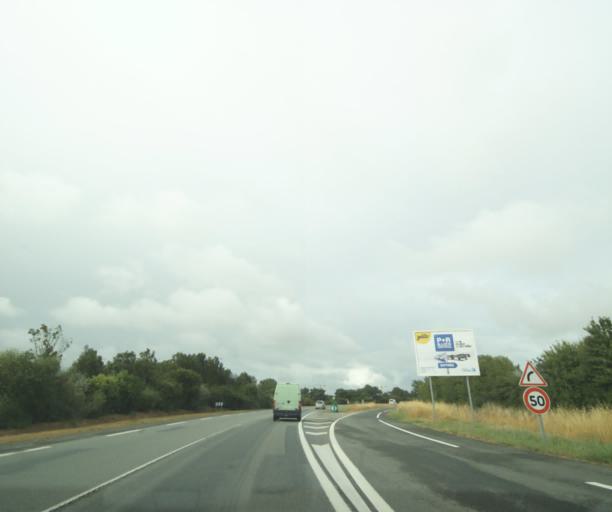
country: FR
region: Poitou-Charentes
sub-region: Departement de la Charente-Maritime
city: Lagord
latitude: 46.1931
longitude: -1.1415
